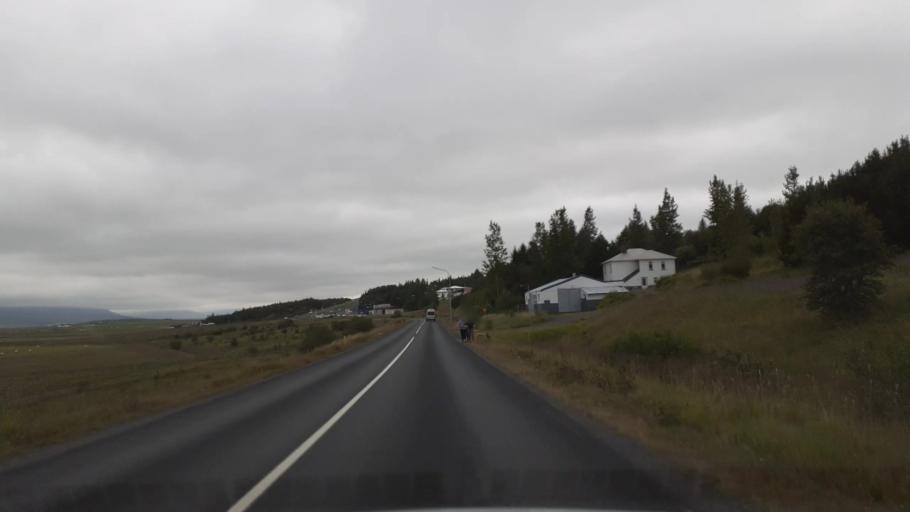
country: IS
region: Northwest
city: Saudarkrokur
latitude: 65.5574
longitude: -19.4517
